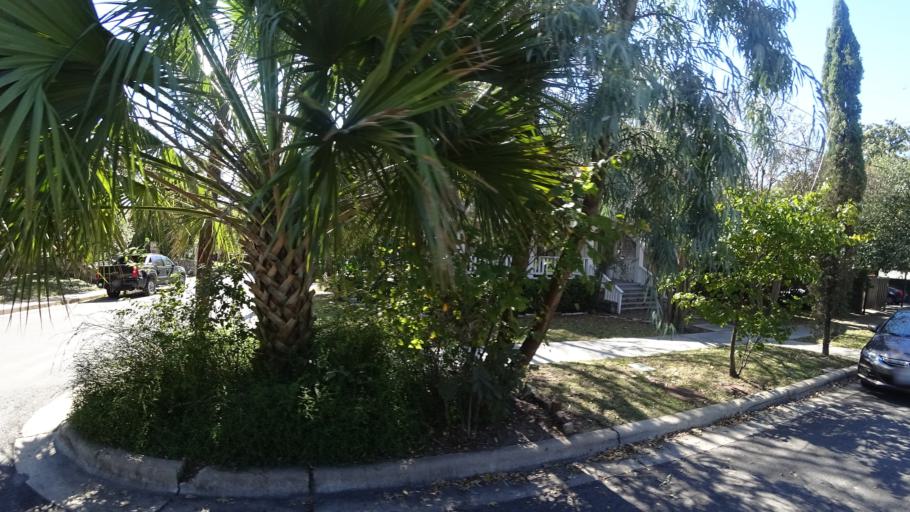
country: US
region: Texas
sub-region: Travis County
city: Austin
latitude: 30.2769
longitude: -97.7594
